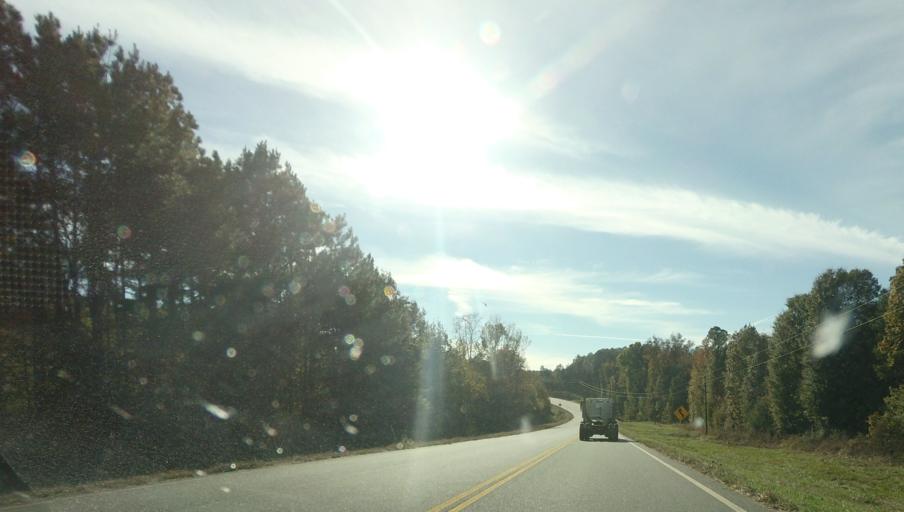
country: US
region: Georgia
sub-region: Talbot County
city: Talbotton
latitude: 32.7031
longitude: -84.4107
